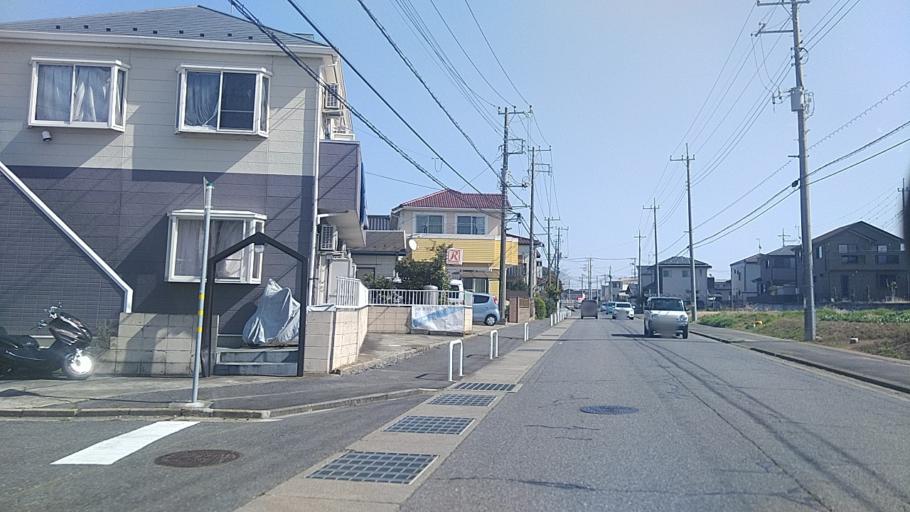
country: JP
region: Ibaraki
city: Ryugasaki
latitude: 35.8540
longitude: 140.1486
